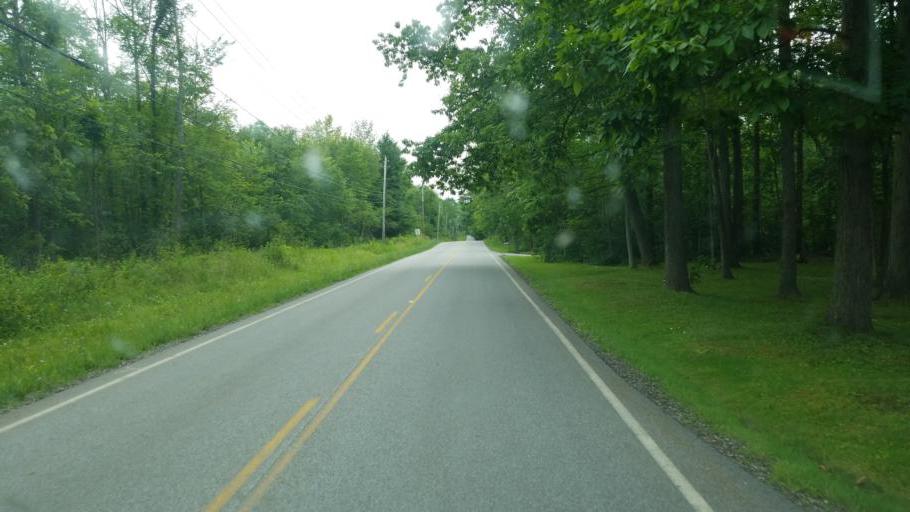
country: US
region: Ohio
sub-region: Geauga County
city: Burton
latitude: 41.4806
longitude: -81.2149
